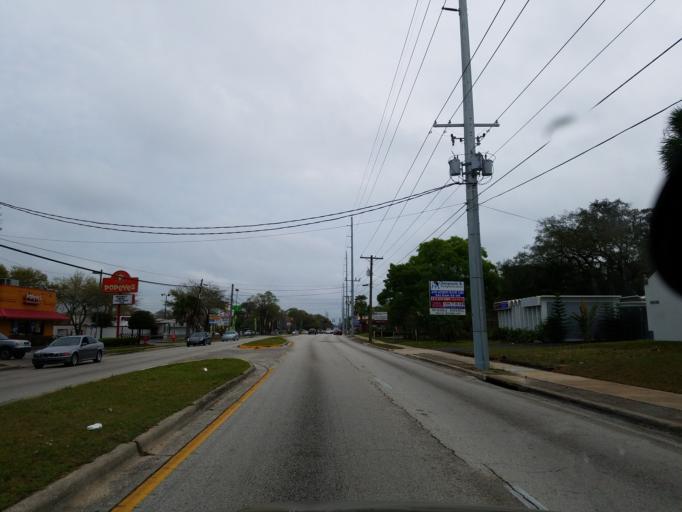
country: US
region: Florida
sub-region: Hillsborough County
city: Egypt Lake-Leto
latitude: 28.0253
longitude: -82.4867
